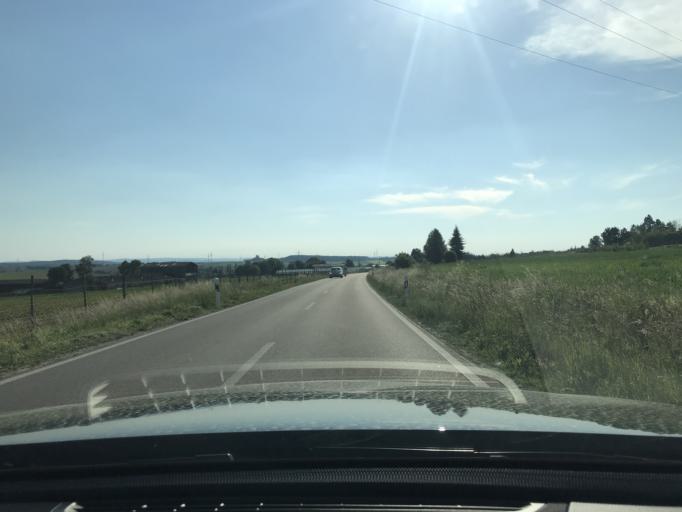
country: DE
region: Baden-Wuerttemberg
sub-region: Regierungsbezirk Stuttgart
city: Schwaikheim
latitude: 48.8914
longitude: 9.3411
